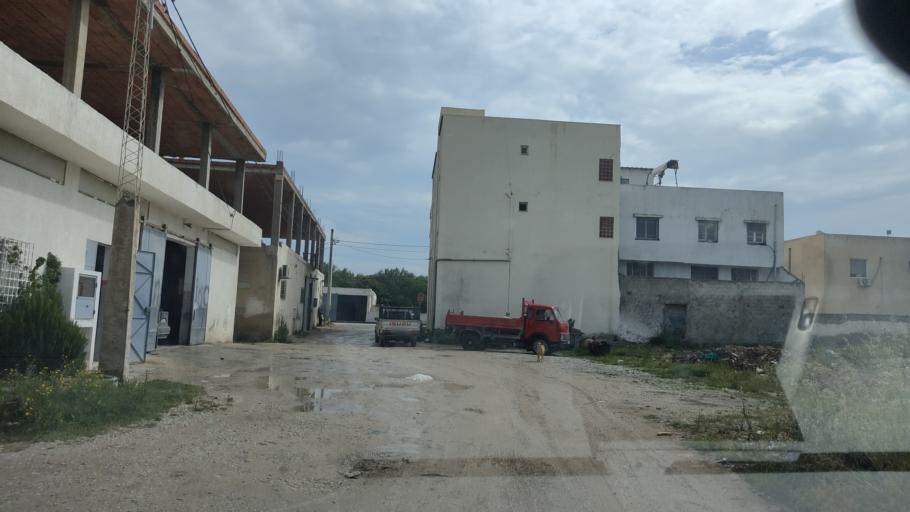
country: TN
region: Ariana
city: Ariana
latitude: 36.8889
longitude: 10.2134
